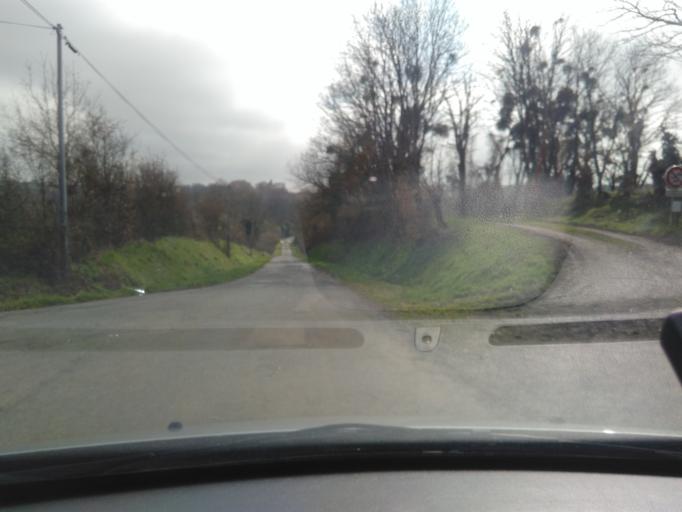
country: FR
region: Pays de la Loire
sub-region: Departement de la Vendee
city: Sainte-Cecile
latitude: 46.7027
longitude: -1.1280
